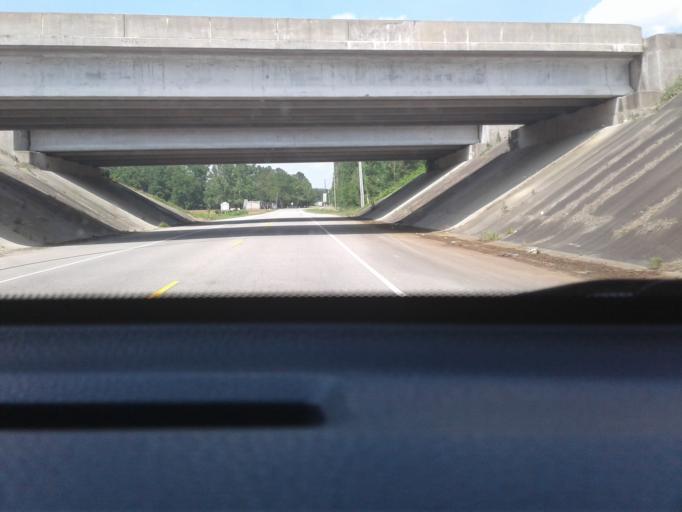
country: US
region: North Carolina
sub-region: Cumberland County
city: Eastover
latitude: 35.1247
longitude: -78.7605
